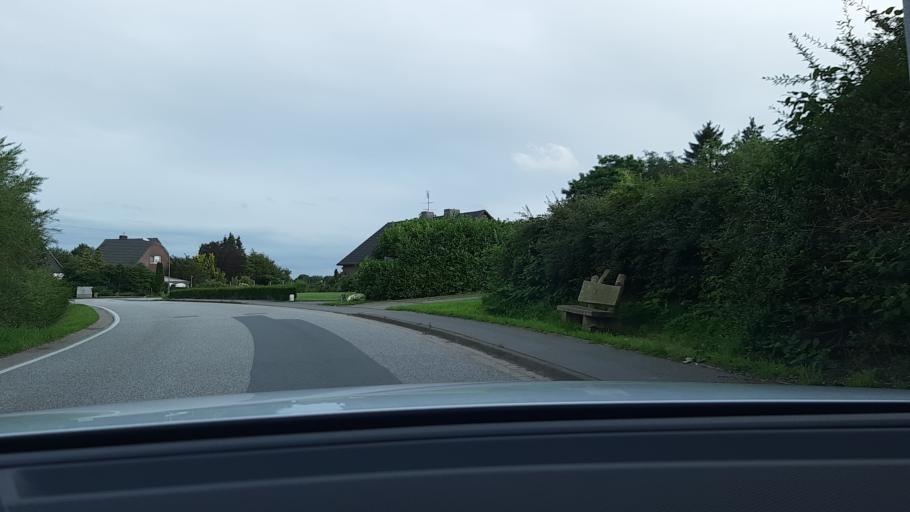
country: DE
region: Schleswig-Holstein
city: Wesenberg
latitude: 53.8520
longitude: 10.5393
